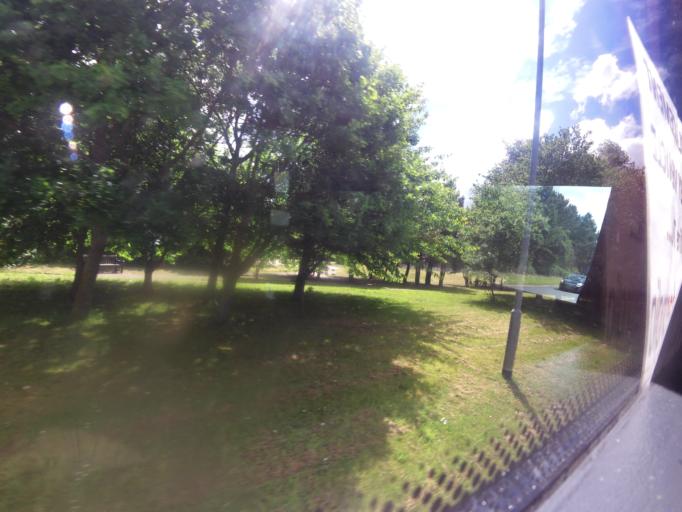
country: GB
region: England
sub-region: Norfolk
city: Cromer
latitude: 52.9258
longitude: 1.2857
